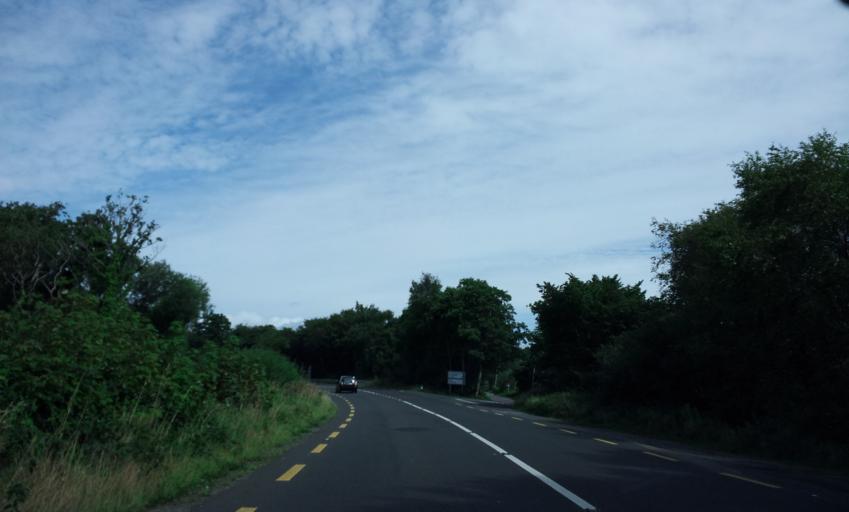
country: IE
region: Munster
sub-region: Ciarrai
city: Killorglin
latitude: 52.0983
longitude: -9.8270
